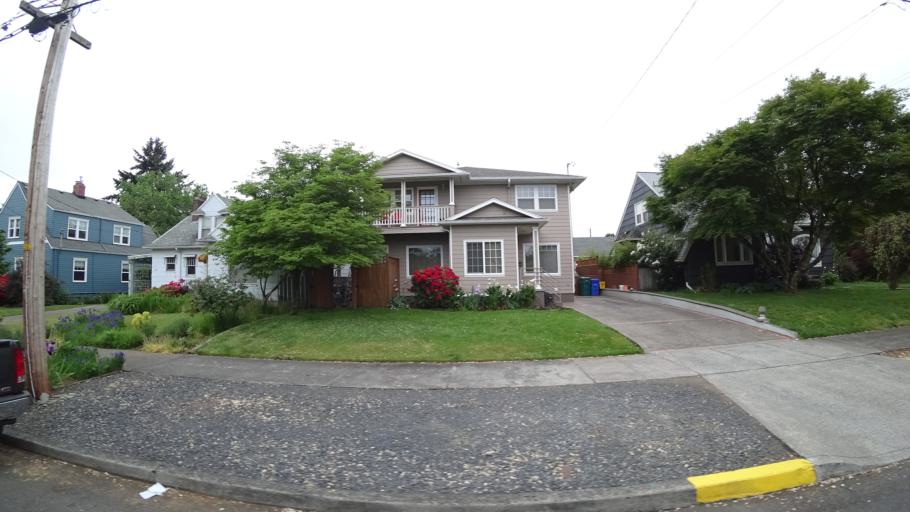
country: US
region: Oregon
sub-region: Multnomah County
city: Portland
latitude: 45.5472
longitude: -122.6137
